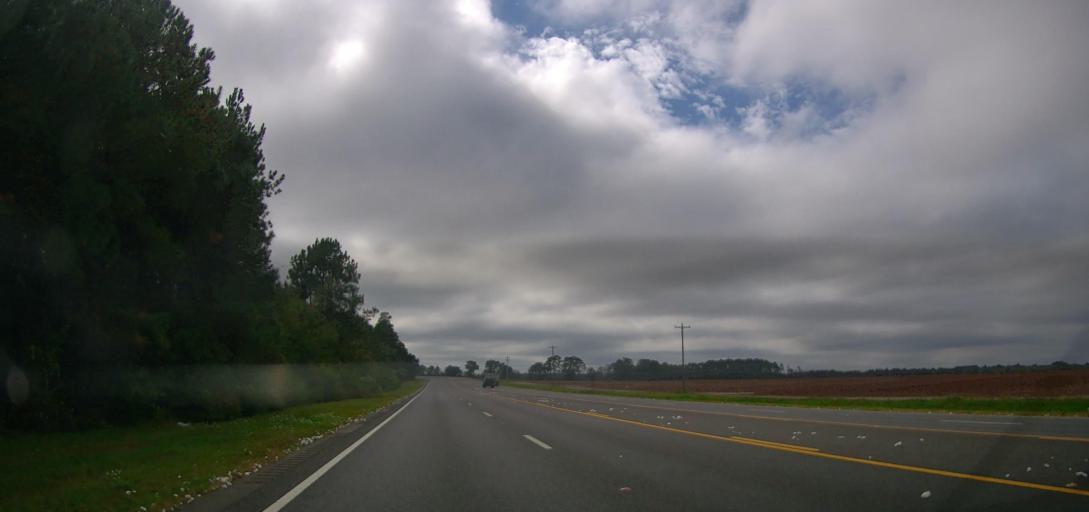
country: US
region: Georgia
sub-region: Colquitt County
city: Moultrie
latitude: 31.0304
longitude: -83.8585
